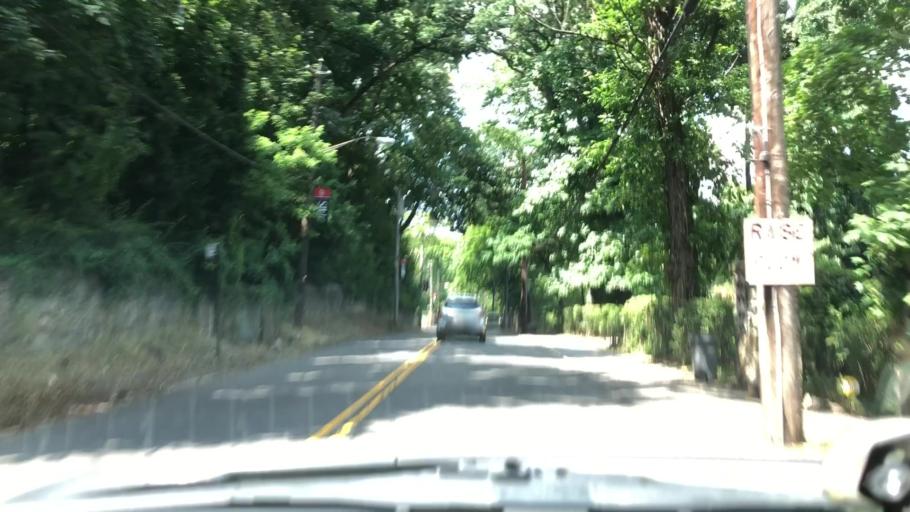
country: US
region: New Jersey
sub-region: Hudson County
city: Bayonne
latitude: 40.6214
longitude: -74.0886
